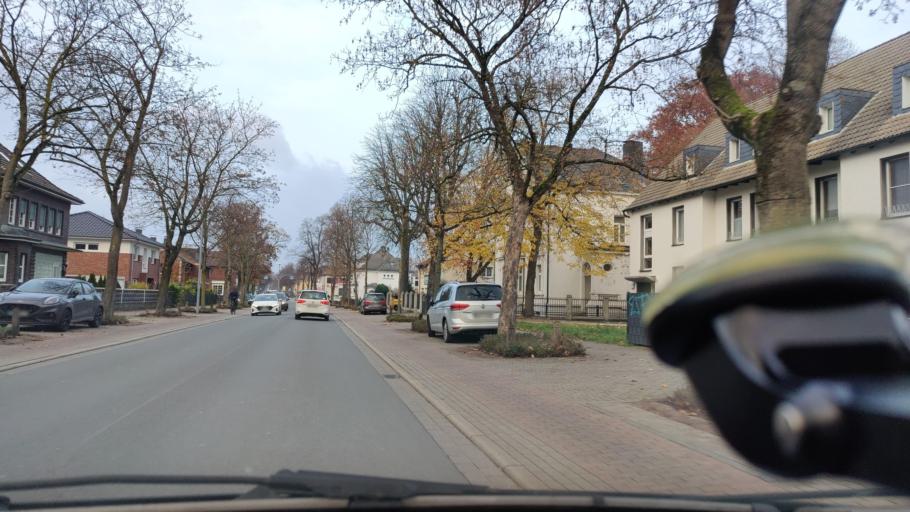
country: DE
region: North Rhine-Westphalia
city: Lunen
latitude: 51.6251
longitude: 7.5260
